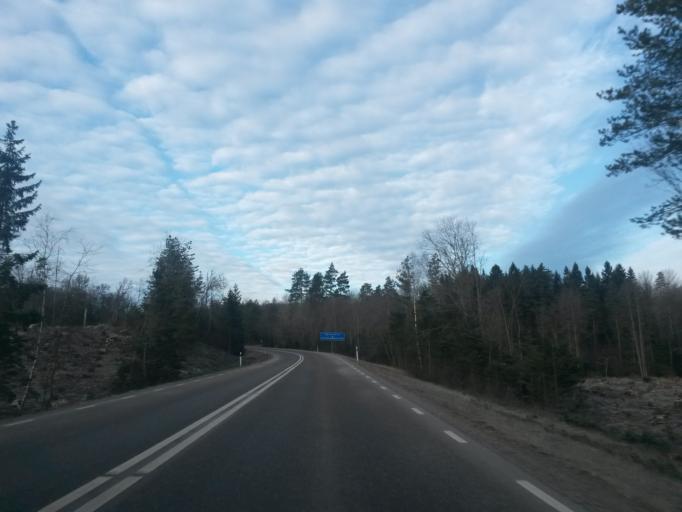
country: SE
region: Vaestra Goetaland
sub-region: Vargarda Kommun
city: Vargarda
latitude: 57.9450
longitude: 12.8365
